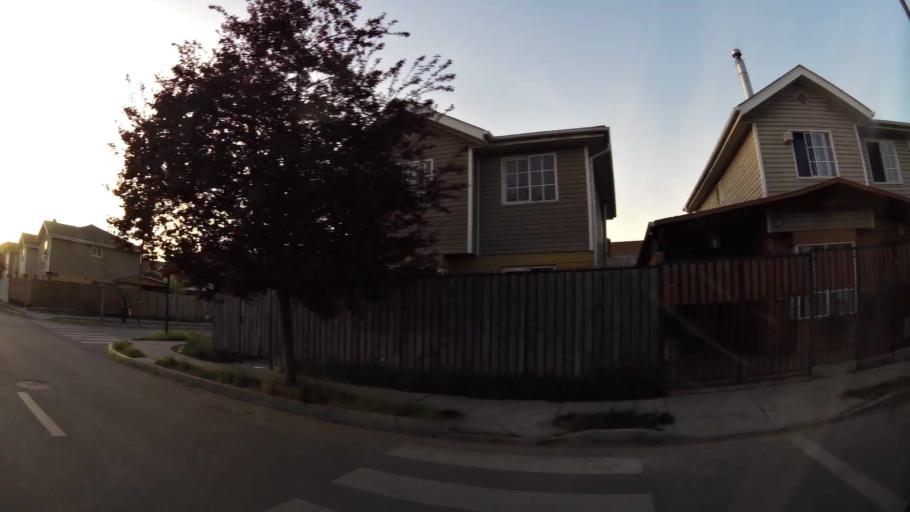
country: CL
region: Santiago Metropolitan
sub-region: Provincia de Cordillera
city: Puente Alto
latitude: -33.5970
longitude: -70.5867
